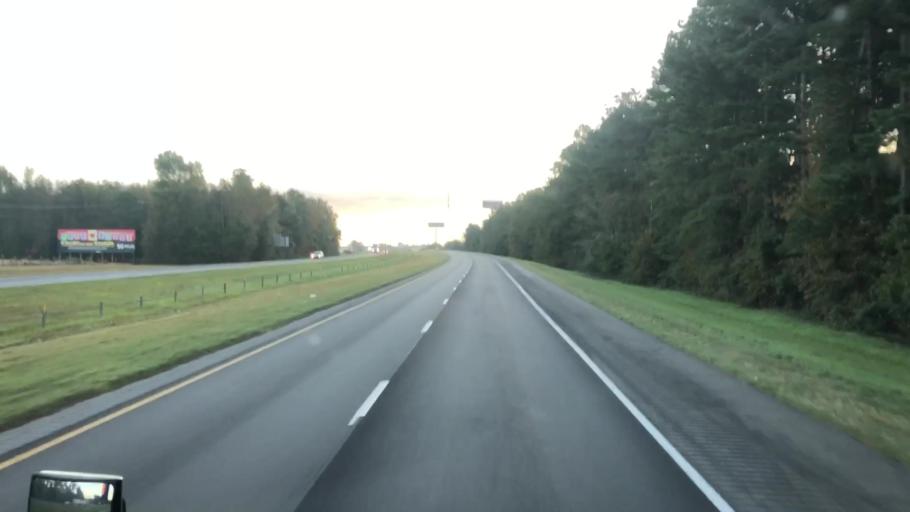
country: US
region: South Carolina
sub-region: Clarendon County
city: Manning
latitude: 33.5958
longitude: -80.3369
